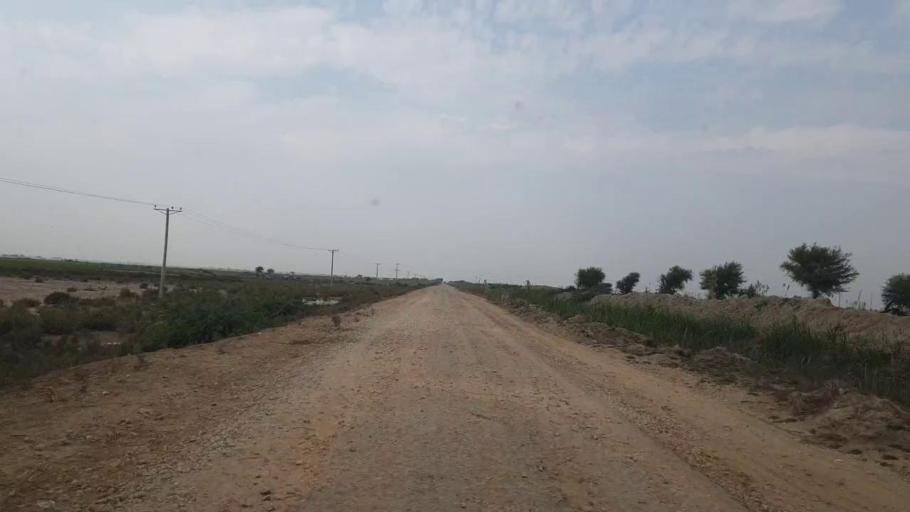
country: PK
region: Sindh
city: Kario
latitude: 24.6145
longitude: 68.5885
